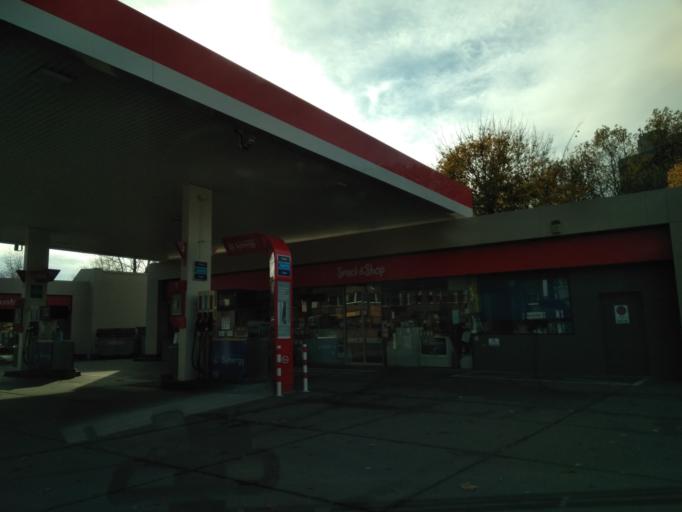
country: DE
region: North Rhine-Westphalia
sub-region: Regierungsbezirk Munster
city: Gladbeck
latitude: 51.5727
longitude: 6.9833
